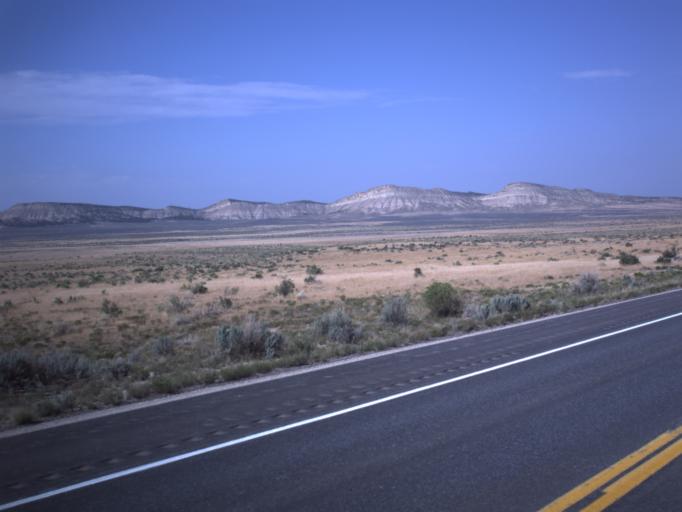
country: US
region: Colorado
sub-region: Rio Blanco County
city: Rangely
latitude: 40.2803
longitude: -109.0702
